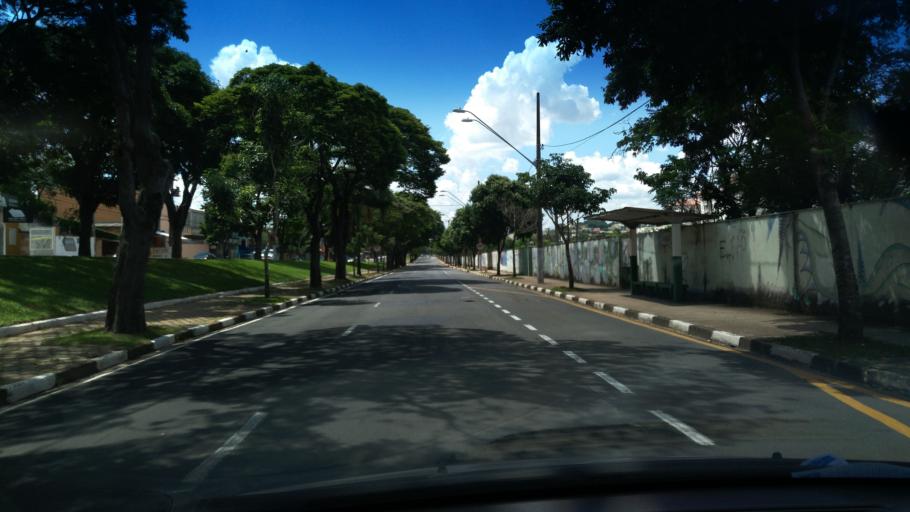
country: BR
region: Sao Paulo
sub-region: Valinhos
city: Valinhos
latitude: -22.9833
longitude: -46.9907
